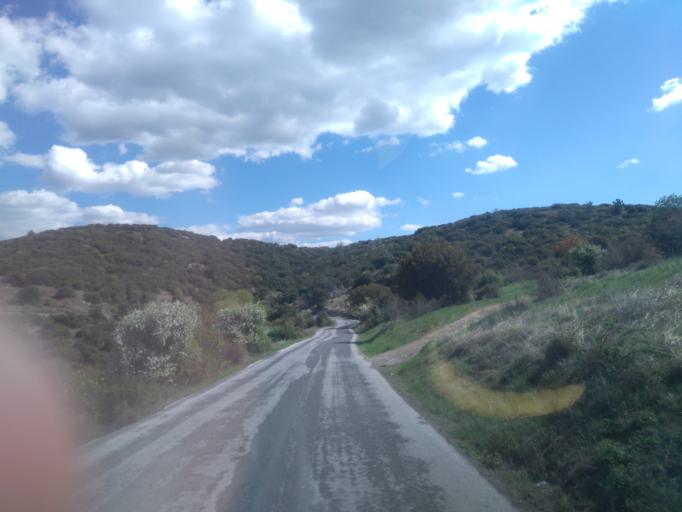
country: GR
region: Central Macedonia
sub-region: Nomos Thessalonikis
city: Asvestochori
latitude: 40.6386
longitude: 23.0144
